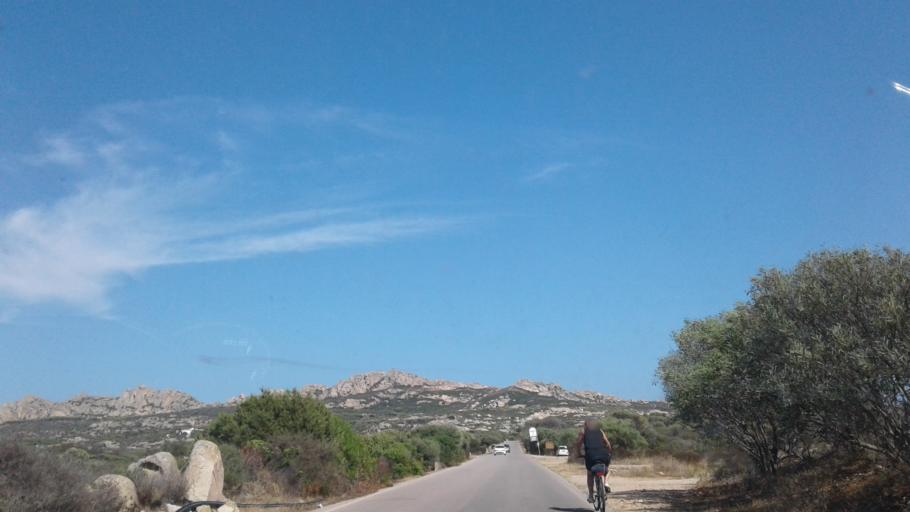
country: IT
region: Sardinia
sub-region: Provincia di Olbia-Tempio
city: La Maddalena
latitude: 41.2151
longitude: 9.4487
